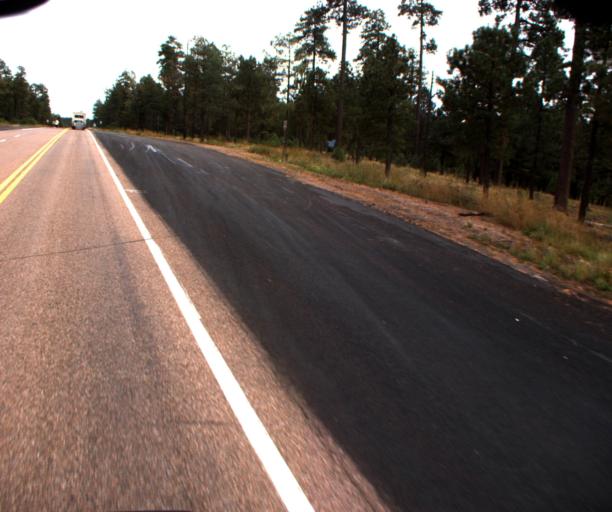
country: US
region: Arizona
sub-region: Navajo County
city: Heber-Overgaard
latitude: 34.3287
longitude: -110.8105
